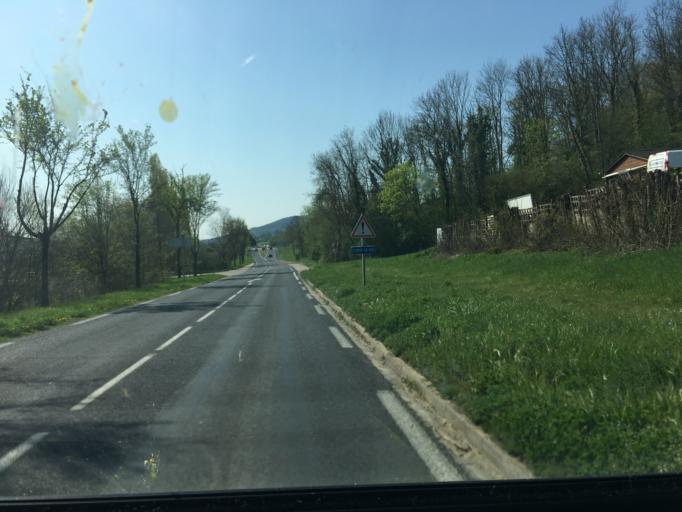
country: FR
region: Lorraine
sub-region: Departement de Meurthe-et-Moselle
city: Norroy-les-Pont-a-Mousson
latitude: 48.9214
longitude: 6.0382
